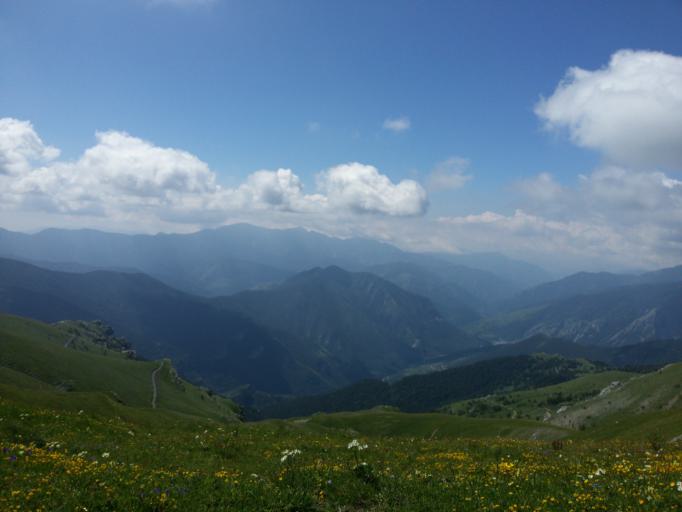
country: IT
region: Piedmont
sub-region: Provincia di Cuneo
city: Limone Piemonte
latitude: 44.1494
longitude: 7.6147
